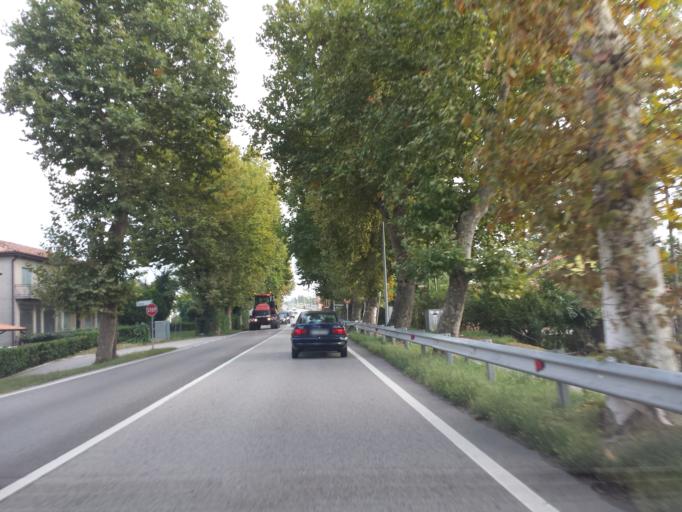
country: IT
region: Veneto
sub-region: Provincia di Padova
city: Boara Pisani
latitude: 45.1090
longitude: 11.7803
